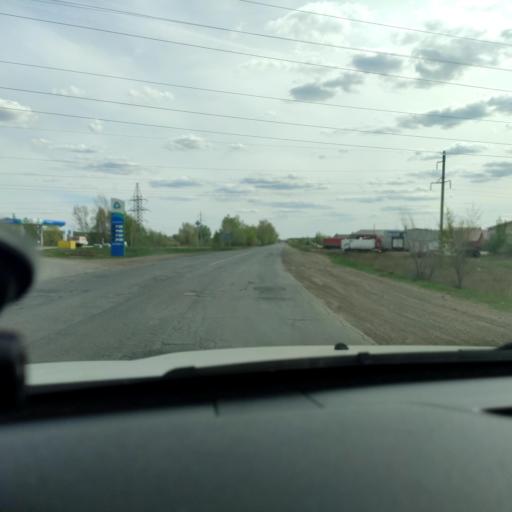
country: RU
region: Samara
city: Kinel'
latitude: 53.2064
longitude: 50.6370
